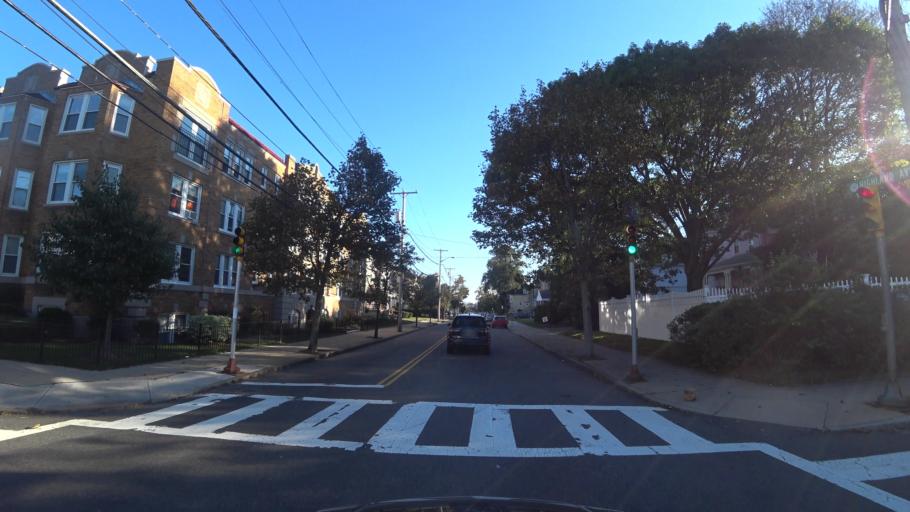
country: US
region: Massachusetts
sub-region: Middlesex County
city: Malden
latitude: 42.4287
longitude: -71.0814
